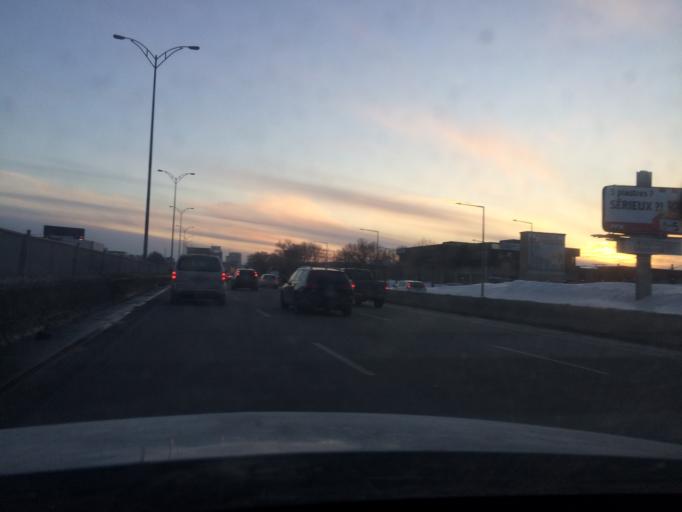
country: CA
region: Quebec
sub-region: Montreal
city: Saint-Leonard
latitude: 45.5762
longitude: -73.5945
